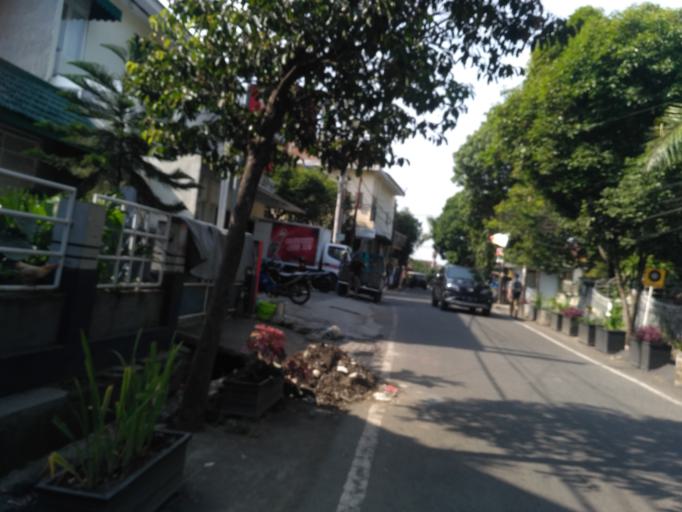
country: ID
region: East Java
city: Malang
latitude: -7.9356
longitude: 112.6069
